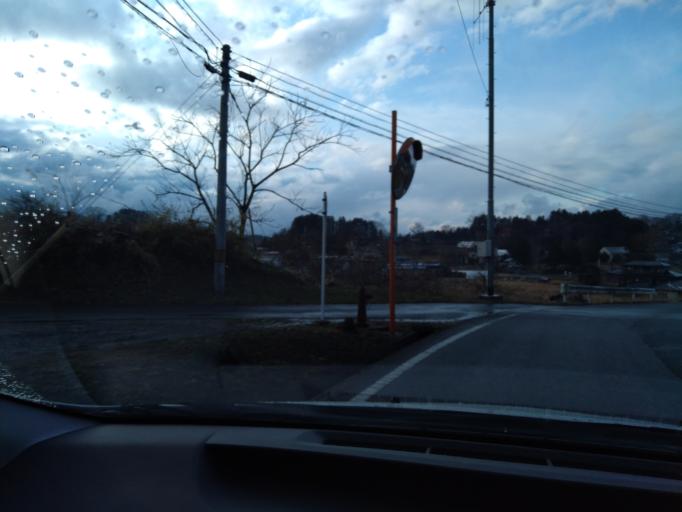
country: JP
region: Iwate
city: Ichinoseki
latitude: 38.7400
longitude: 141.1209
